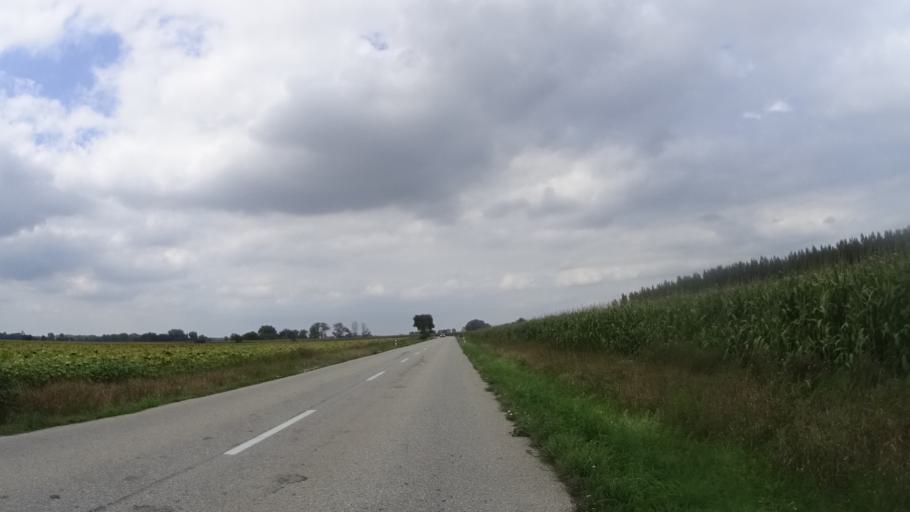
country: HU
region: Gyor-Moson-Sopron
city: Bony
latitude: 47.7580
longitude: 17.8451
